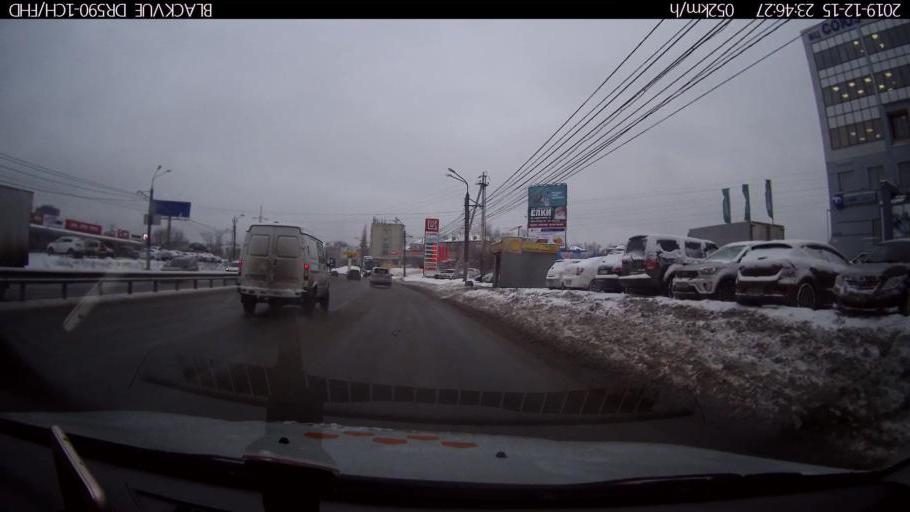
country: RU
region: Nizjnij Novgorod
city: Nizhniy Novgorod
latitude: 56.2970
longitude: 43.9316
